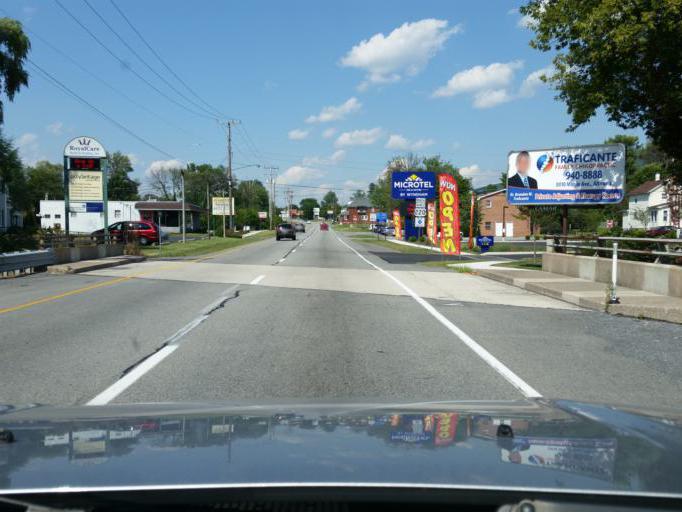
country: US
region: Pennsylvania
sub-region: Blair County
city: Altoona
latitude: 40.5003
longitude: -78.3889
